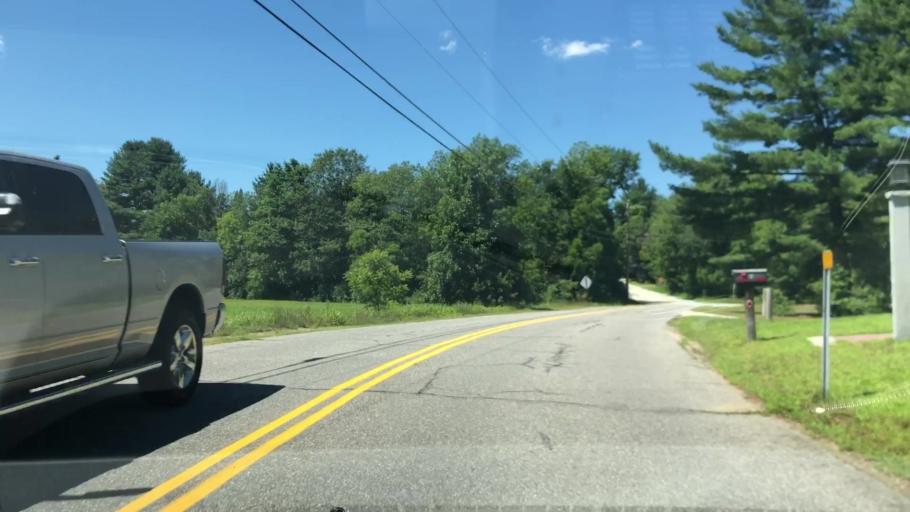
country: US
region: New Hampshire
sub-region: Hillsborough County
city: Milford
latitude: 42.8300
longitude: -71.5850
